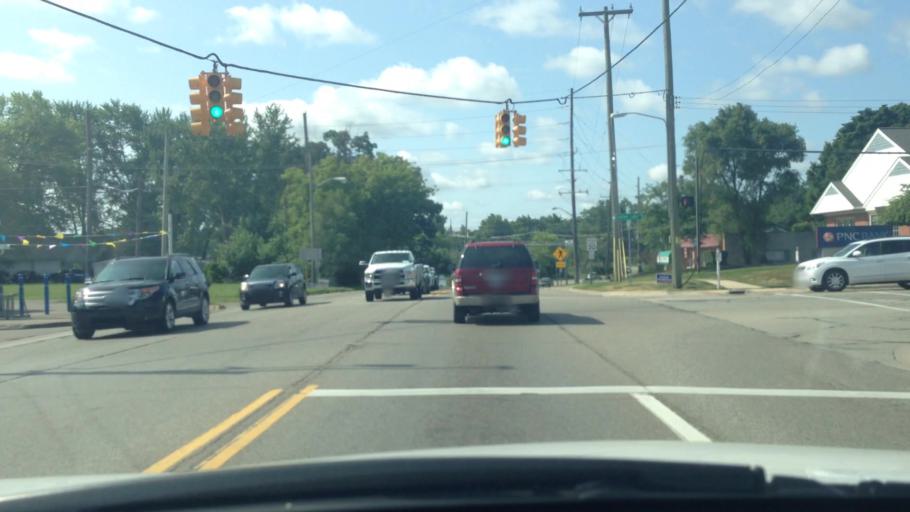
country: US
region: Michigan
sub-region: Oakland County
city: Wolverine Lake
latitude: 42.6134
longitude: -83.4468
